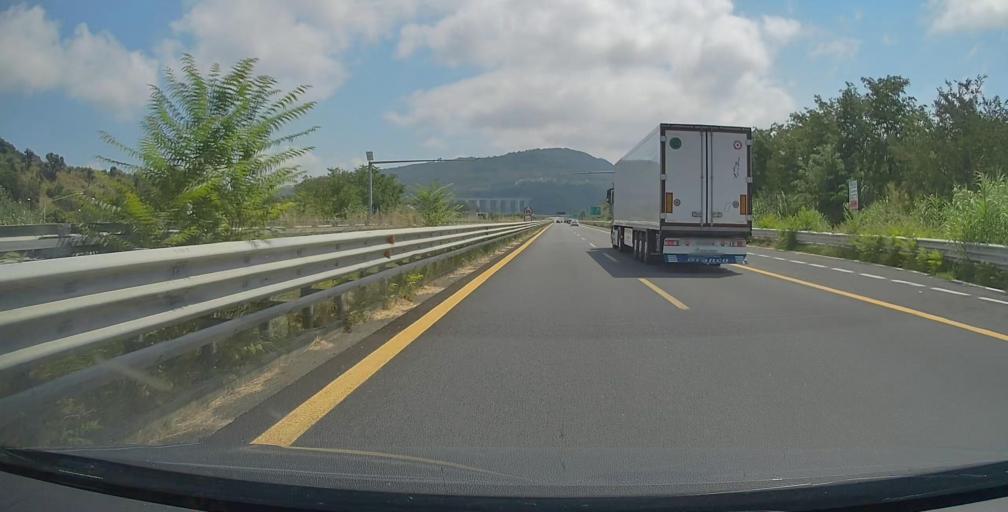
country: IT
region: Calabria
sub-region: Provincia di Vibo-Valentia
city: Pizzo
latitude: 38.7827
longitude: 16.2182
